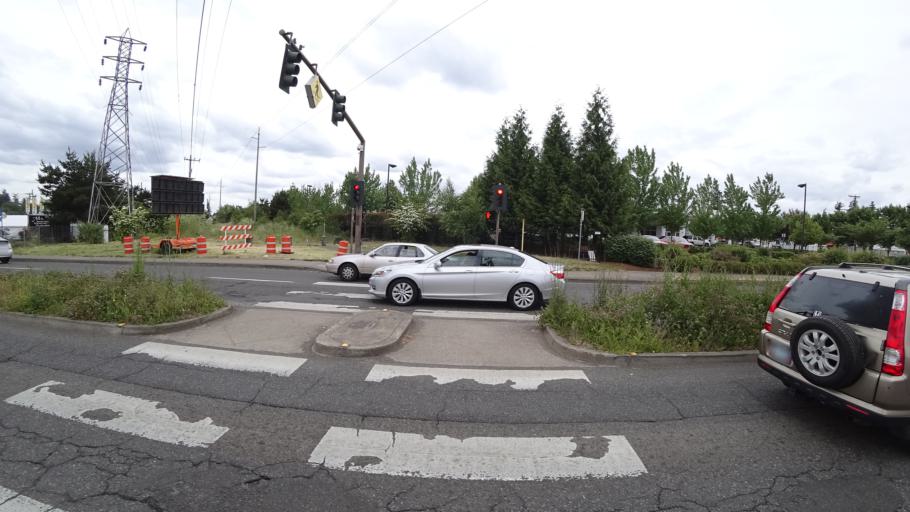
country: US
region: Oregon
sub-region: Multnomah County
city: Lents
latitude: 45.4645
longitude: -122.5790
